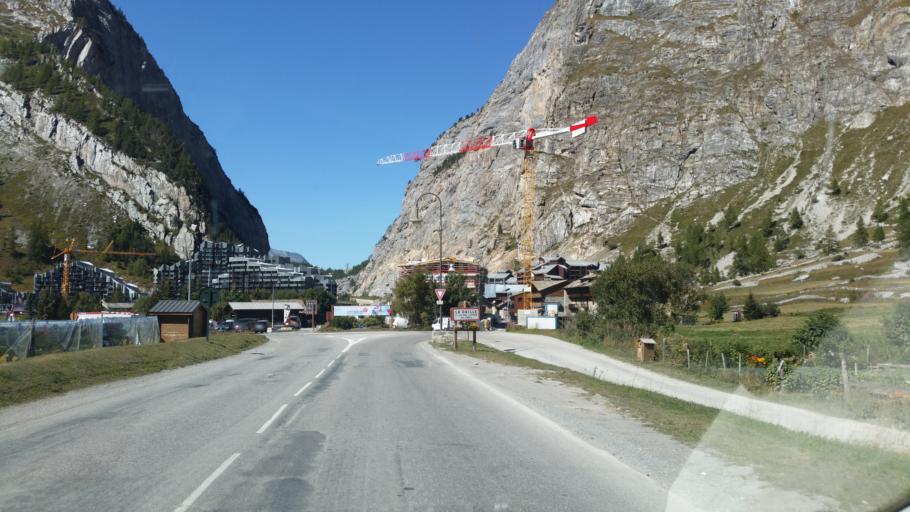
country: FR
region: Rhone-Alpes
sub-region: Departement de la Savoie
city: Val-d'Isere
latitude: 45.4592
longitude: 6.9668
